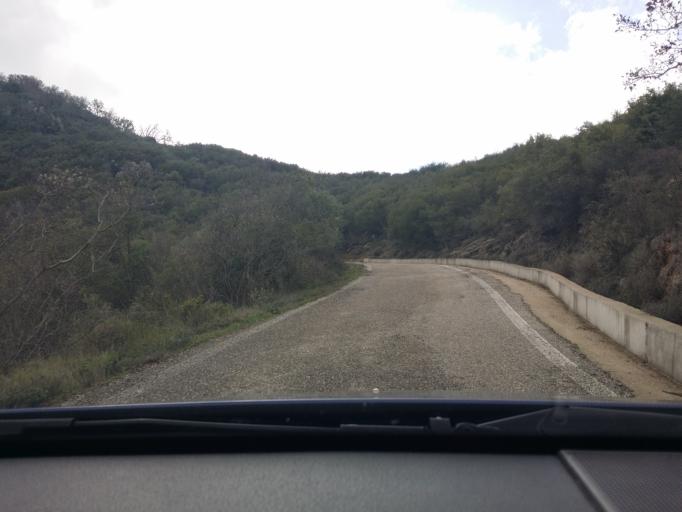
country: GR
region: West Greece
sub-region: Nomos Aitolias kai Akarnanias
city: Fitiai
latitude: 38.6540
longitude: 21.1962
